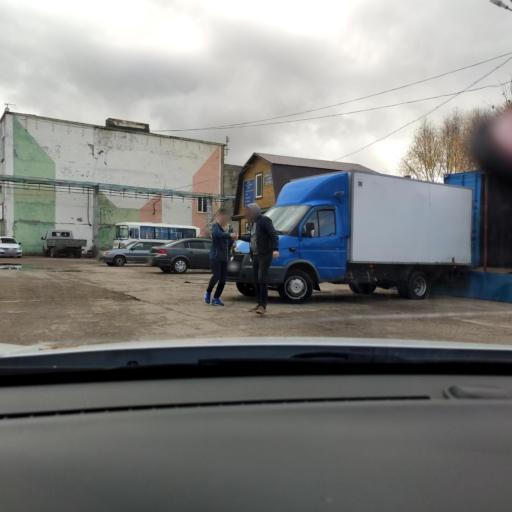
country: RU
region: Tatarstan
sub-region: Gorod Kazan'
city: Kazan
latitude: 55.7775
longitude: 49.1816
